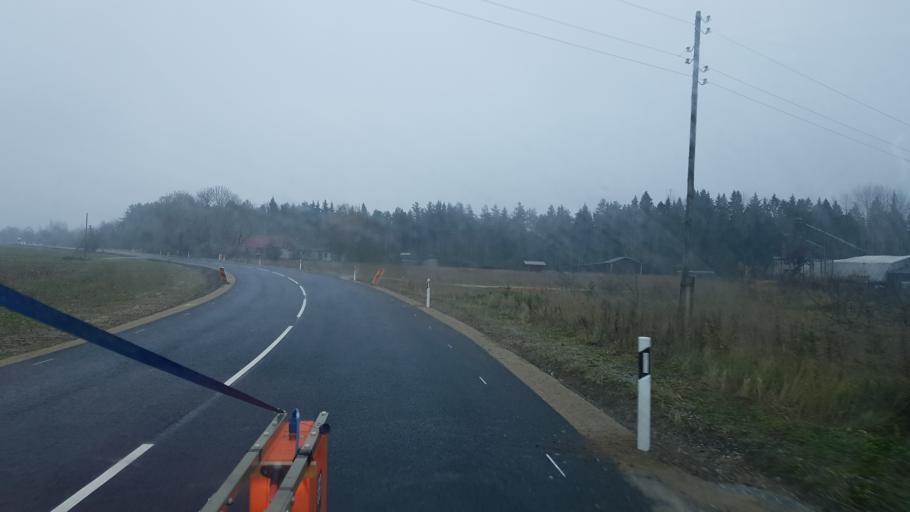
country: EE
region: Raplamaa
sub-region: Kohila vald
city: Kohila
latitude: 59.1754
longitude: 24.8351
